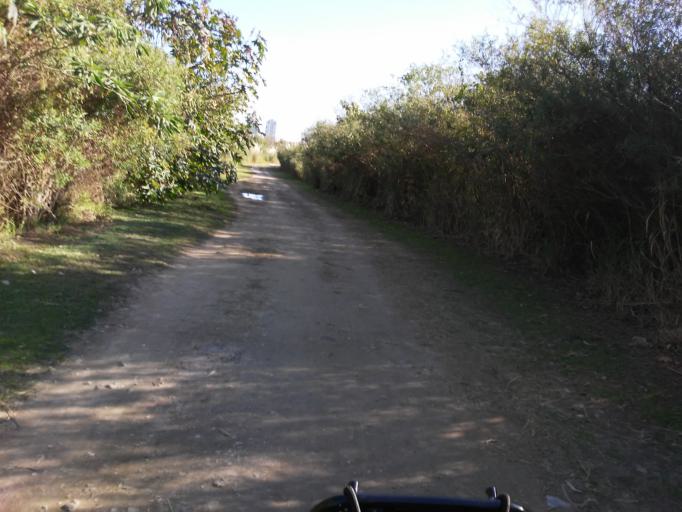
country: AR
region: Buenos Aires F.D.
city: Buenos Aires
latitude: -34.6169
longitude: -58.3433
